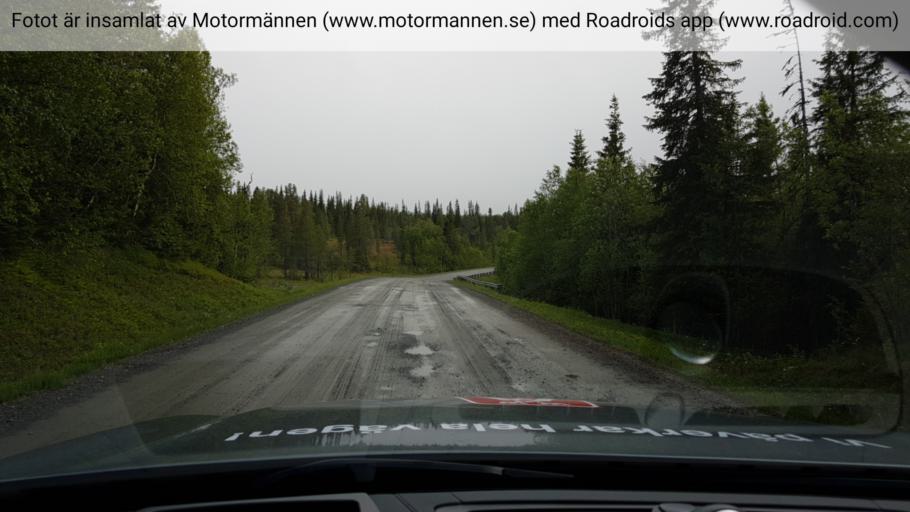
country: NO
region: Nord-Trondelag
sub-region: Snasa
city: Snaase
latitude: 63.7039
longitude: 12.3491
